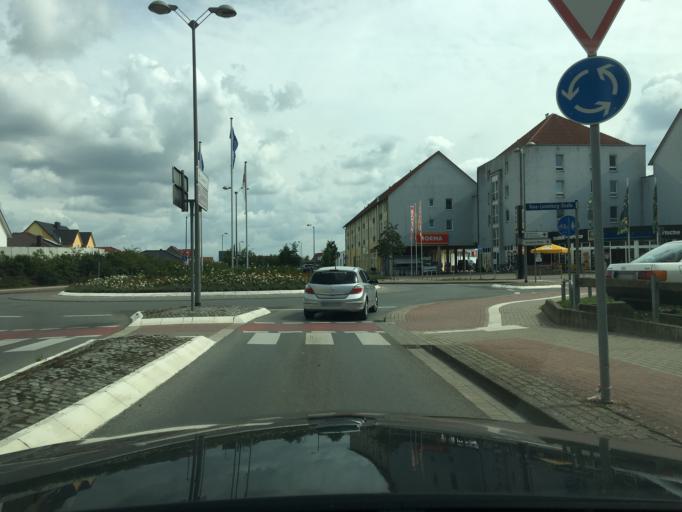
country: DE
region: Mecklenburg-Vorpommern
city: Waren
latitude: 53.5097
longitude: 12.7015
